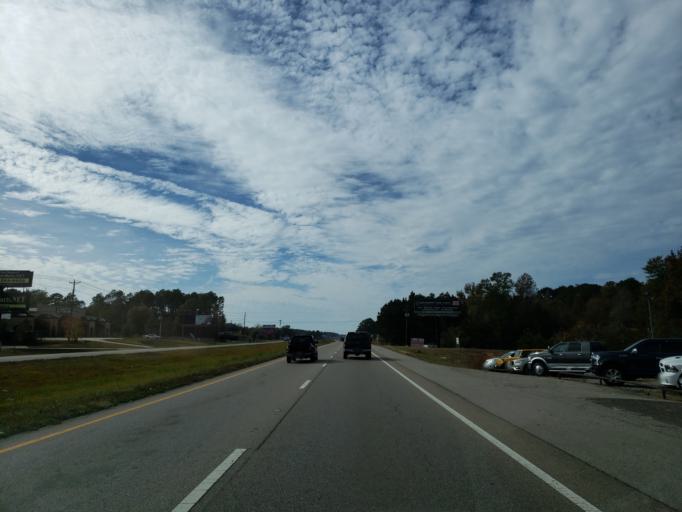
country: US
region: Mississippi
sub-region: Lamar County
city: West Hattiesburg
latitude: 31.3173
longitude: -89.4232
